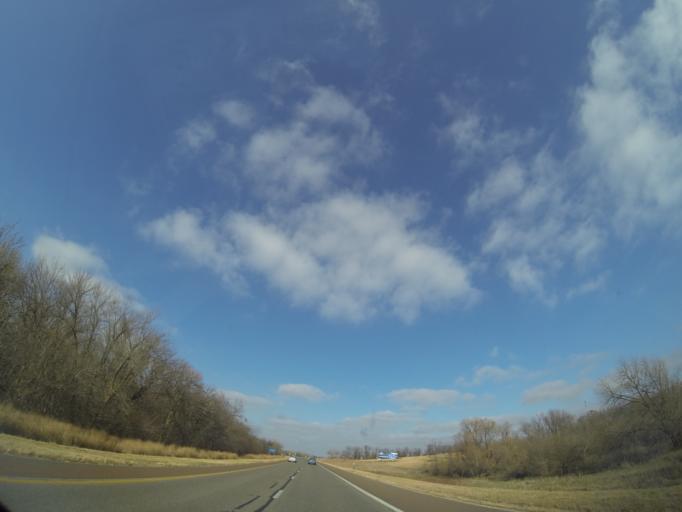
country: US
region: Kansas
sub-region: McPherson County
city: Lindsborg
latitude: 38.4759
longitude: -97.6198
